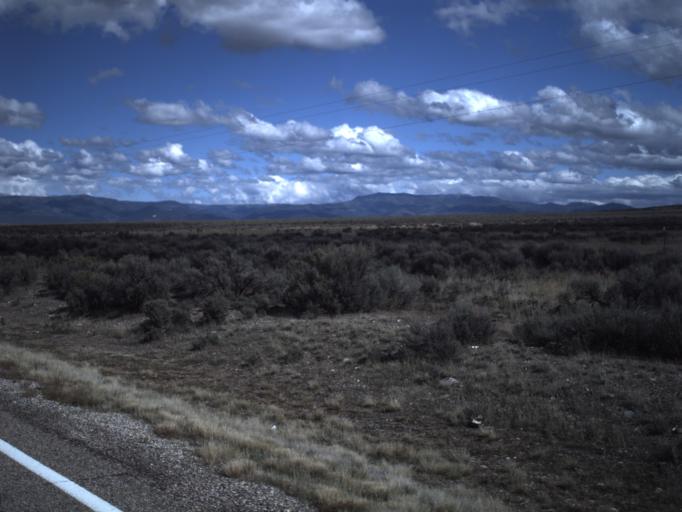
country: US
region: Utah
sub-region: Beaver County
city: Beaver
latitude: 38.2203
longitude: -112.8171
